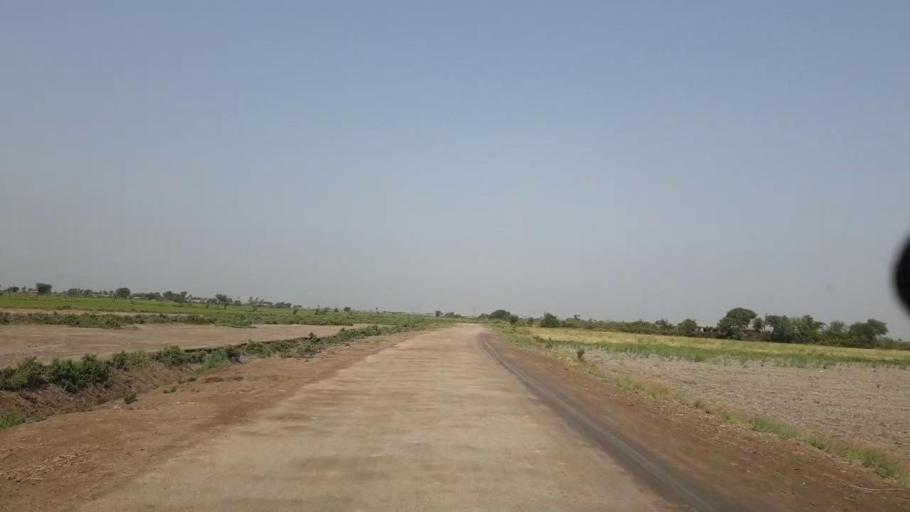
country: PK
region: Sindh
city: Matli
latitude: 25.0687
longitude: 68.6904
